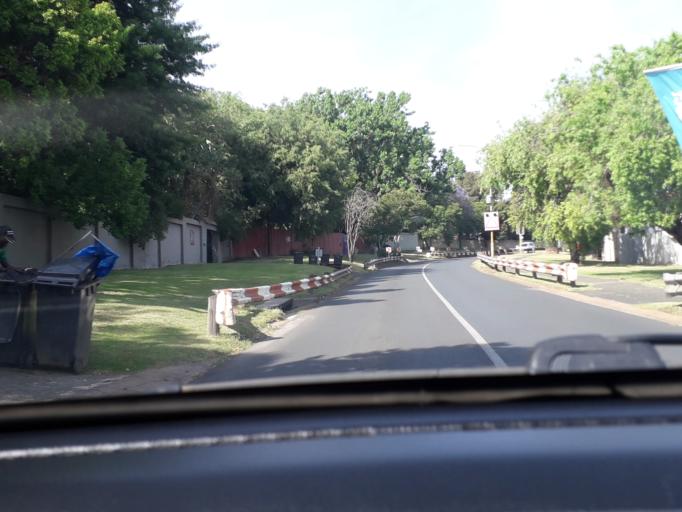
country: ZA
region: Gauteng
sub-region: City of Johannesburg Metropolitan Municipality
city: Modderfontein
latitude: -26.1377
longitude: 28.1031
